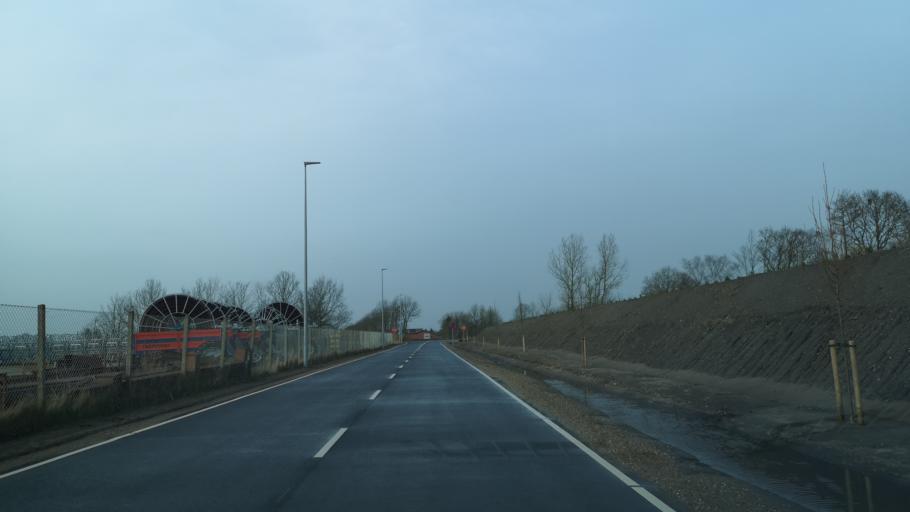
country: DK
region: Central Jutland
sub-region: Ikast-Brande Kommune
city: Brande
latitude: 56.0059
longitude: 9.1198
